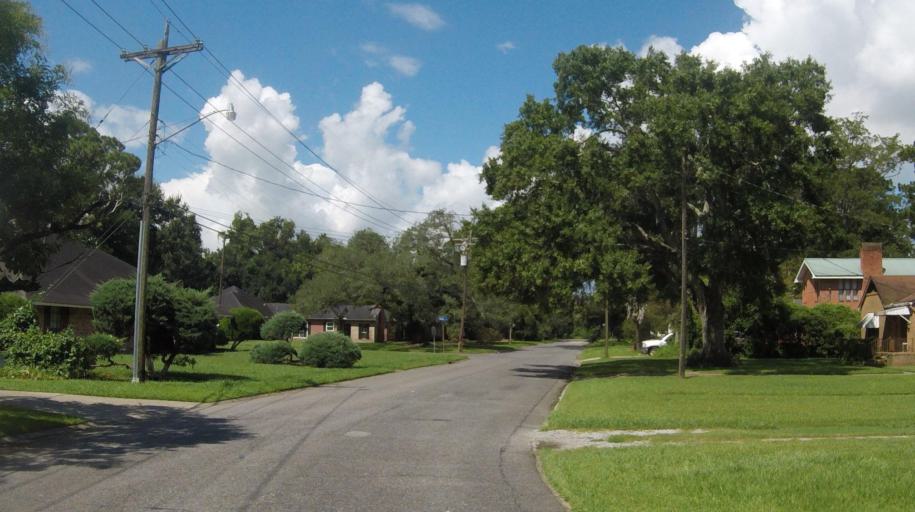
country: US
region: Louisiana
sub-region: West Baton Rouge Parish
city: Port Allen
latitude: 30.4290
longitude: -91.1853
